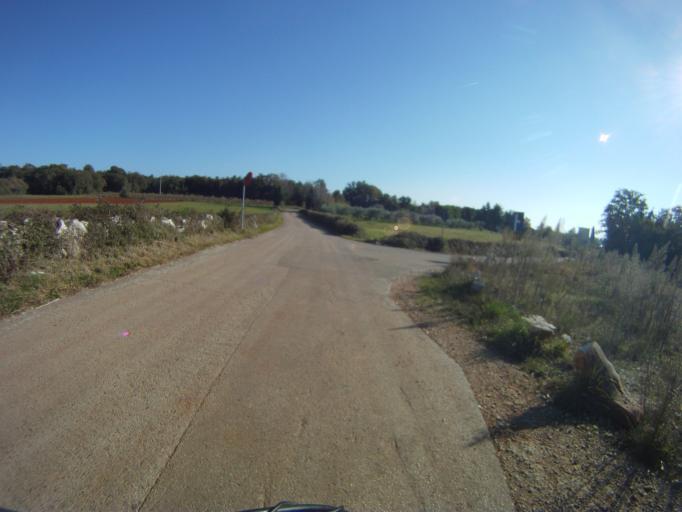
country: HR
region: Istarska
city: Umag
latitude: 45.3959
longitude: 13.5363
